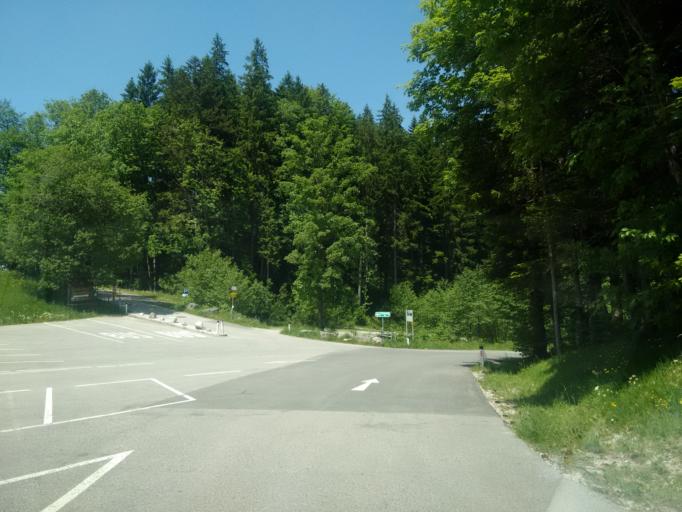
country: AT
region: Upper Austria
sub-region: Politischer Bezirk Kirchdorf an der Krems
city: Rossleithen
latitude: 47.6915
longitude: 14.2973
